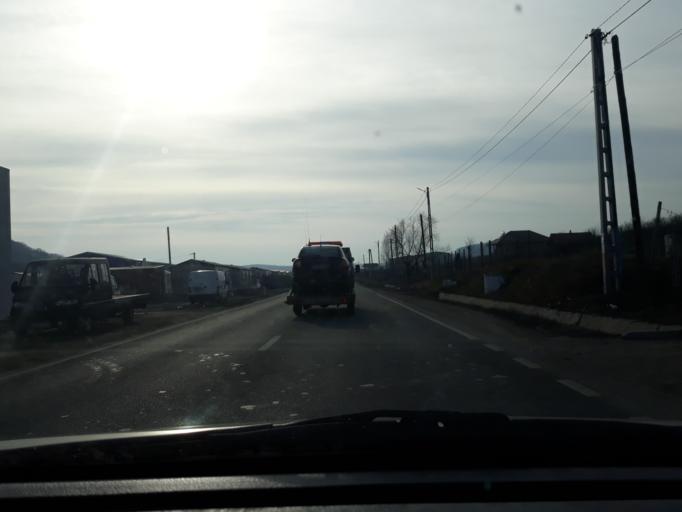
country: RO
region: Salaj
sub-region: Comuna Hereclean
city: Hereclean
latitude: 47.2360
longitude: 22.9837
